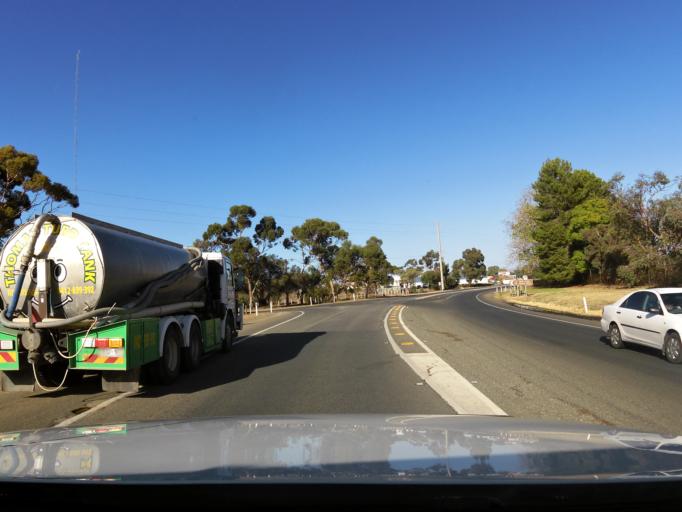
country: AU
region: South Australia
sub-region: Berri and Barmera
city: Berri
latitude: -34.2636
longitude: 140.6139
